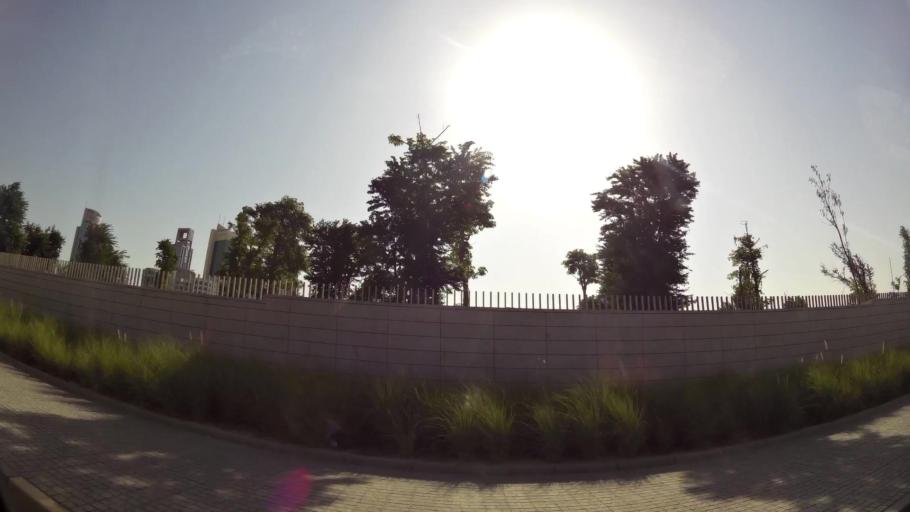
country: KW
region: Al Asimah
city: Ash Shamiyah
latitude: 29.3627
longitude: 47.9576
